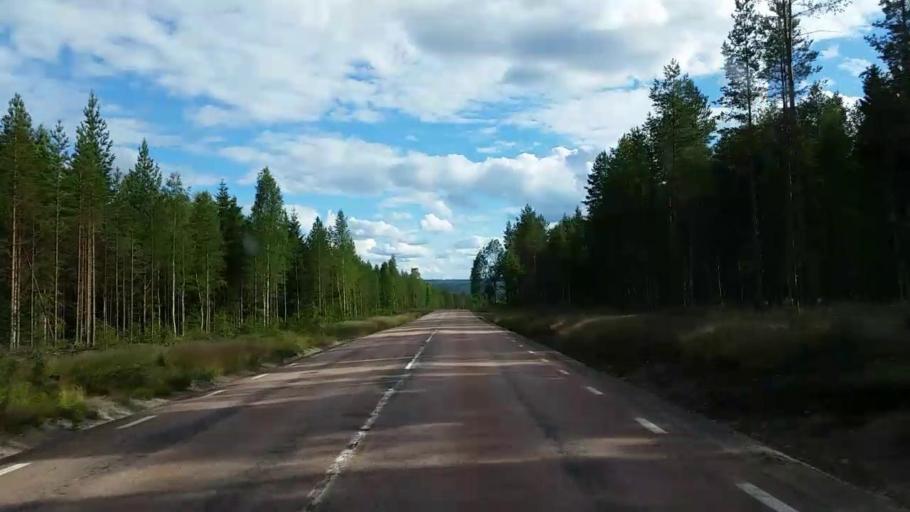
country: SE
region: Gaevleborg
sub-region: Ljusdals Kommun
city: Farila
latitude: 61.9487
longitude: 15.8845
